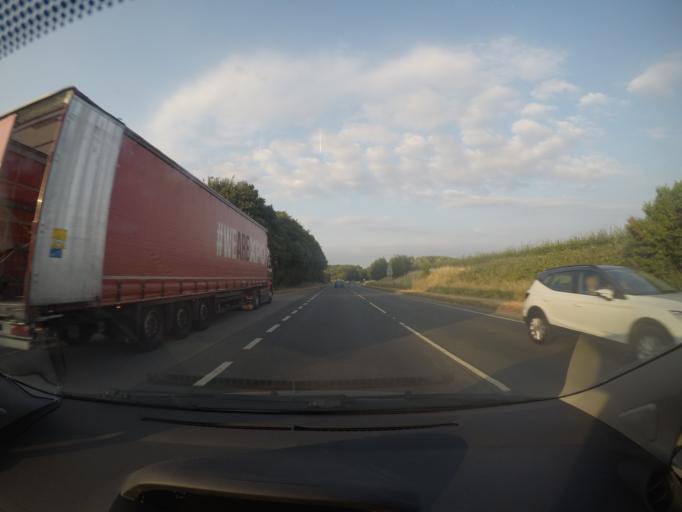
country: GB
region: England
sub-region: City of York
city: Haxby
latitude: 54.0038
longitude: -1.0644
